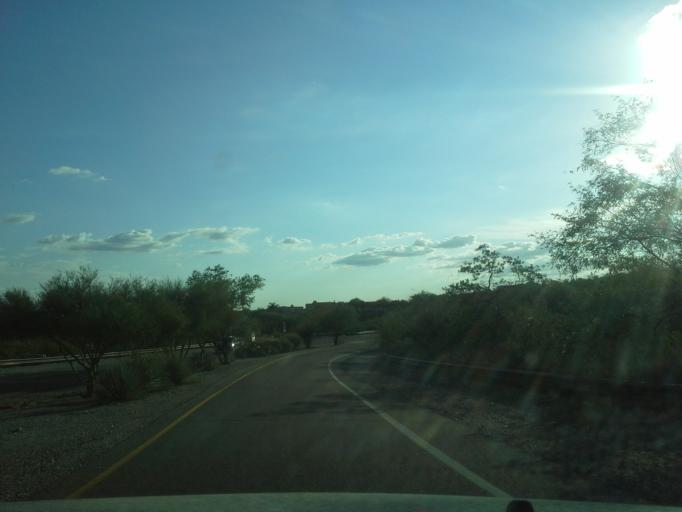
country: US
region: Arizona
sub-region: Pima County
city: Catalina Foothills
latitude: 32.3283
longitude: -110.8645
